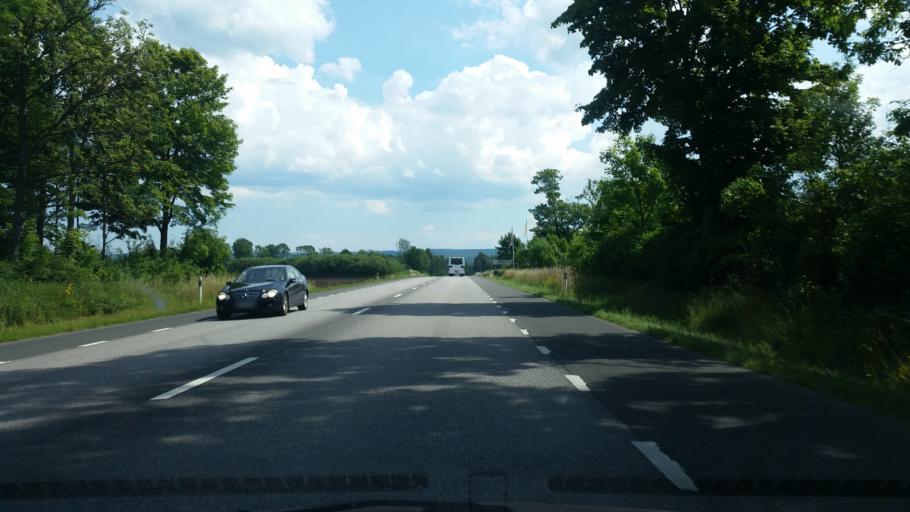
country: SE
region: Vaestra Goetaland
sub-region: Skara Kommun
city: Axvall
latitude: 58.3983
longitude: 13.6037
